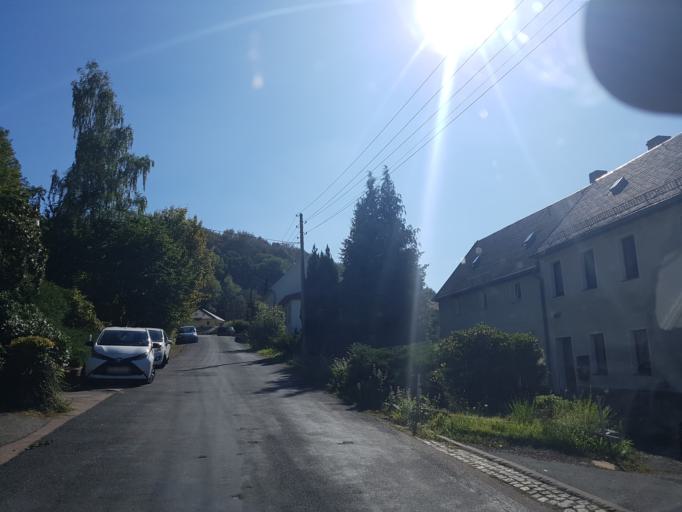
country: DE
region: Saxony
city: Kriebstein
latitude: 51.0480
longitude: 13.0210
